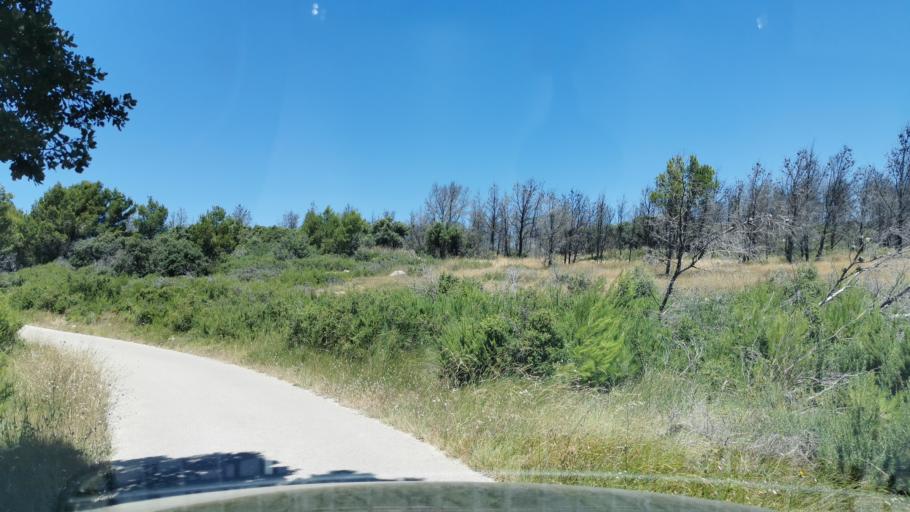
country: FR
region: Languedoc-Roussillon
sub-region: Departement de l'Aude
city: Peyriac-de-Mer
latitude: 43.1068
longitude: 2.9604
